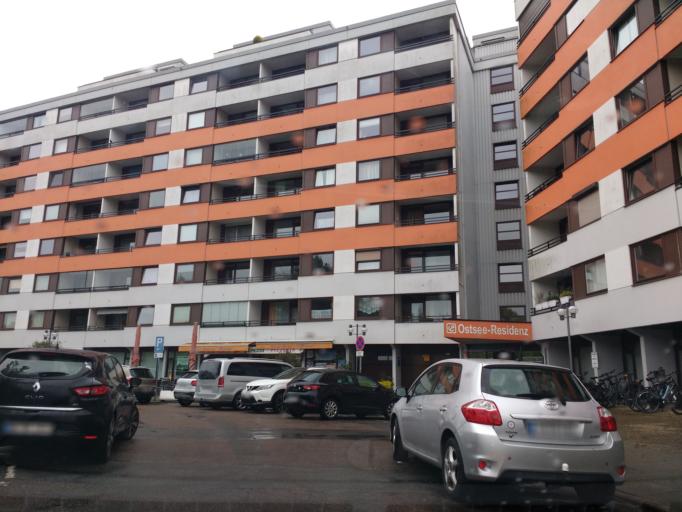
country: DE
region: Schleswig-Holstein
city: Damp
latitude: 54.5814
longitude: 10.0217
